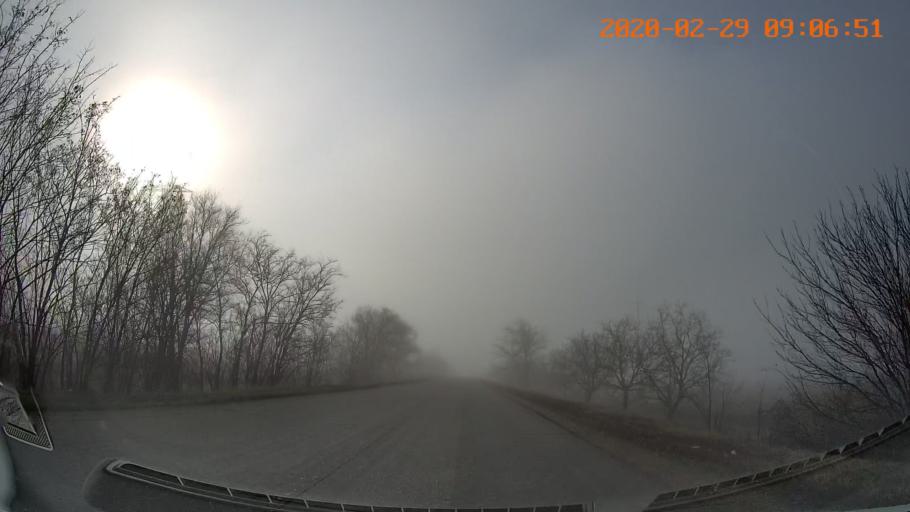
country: MD
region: Telenesti
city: Tiraspolul Nou
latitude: 46.8701
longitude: 29.7464
